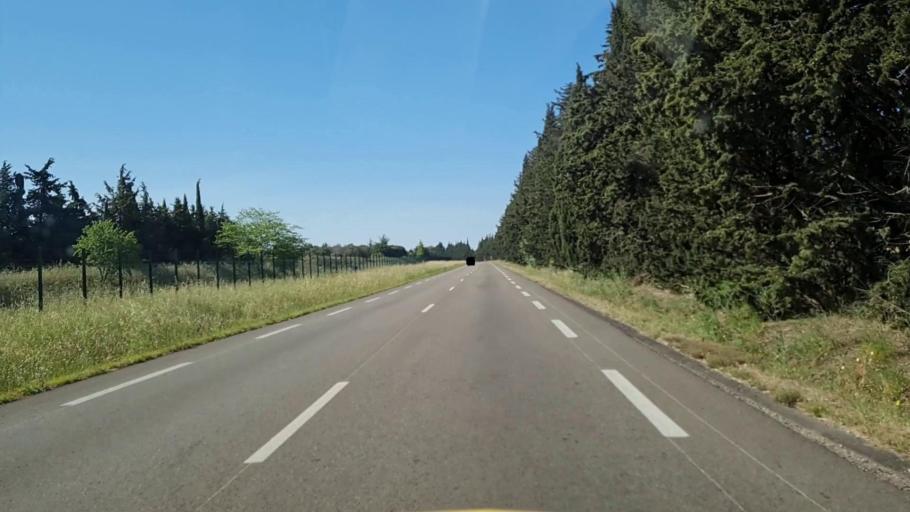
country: FR
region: Languedoc-Roussillon
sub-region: Departement du Gard
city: Garons
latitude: 43.7566
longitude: 4.4062
